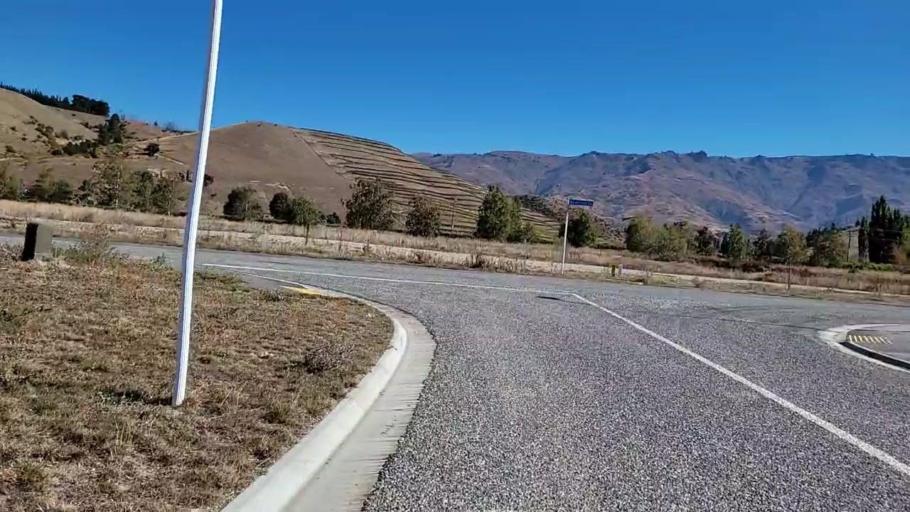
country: NZ
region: Otago
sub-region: Queenstown-Lakes District
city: Wanaka
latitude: -44.9767
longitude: 169.2378
